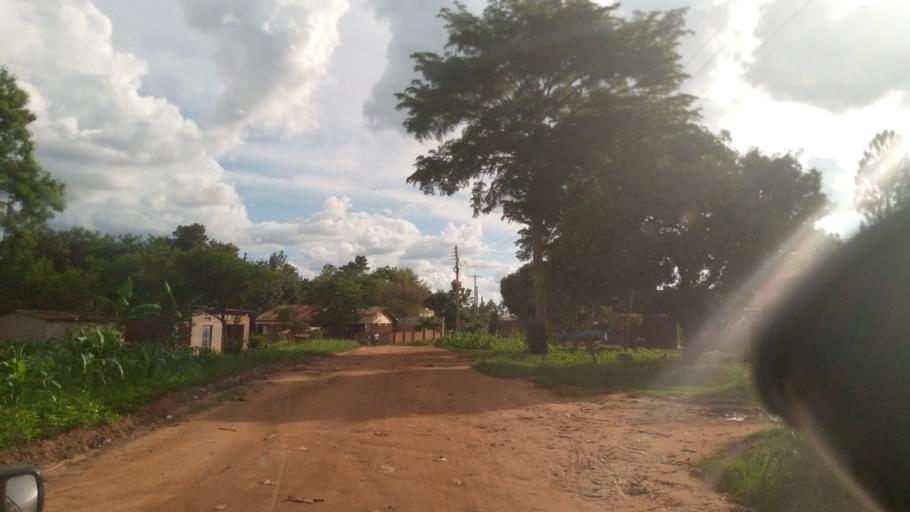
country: UG
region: Northern Region
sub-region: Lira District
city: Lira
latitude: 2.2266
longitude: 32.8916
